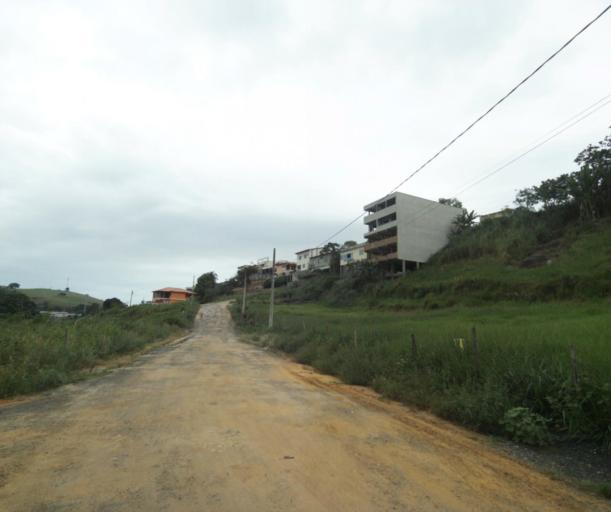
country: BR
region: Espirito Santo
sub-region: Iconha
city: Iconha
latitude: -20.7879
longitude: -40.8124
